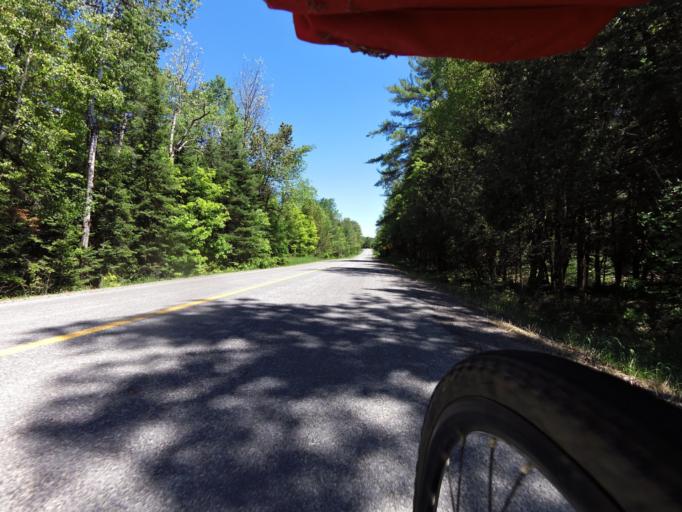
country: CA
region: Ontario
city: Arnprior
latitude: 45.1607
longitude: -76.4354
